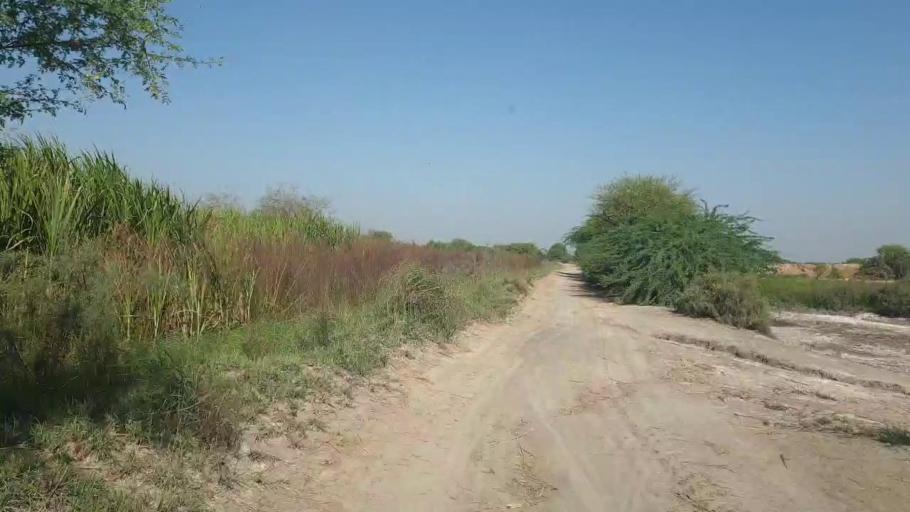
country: PK
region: Sindh
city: Talhar
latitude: 24.8210
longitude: 68.7835
